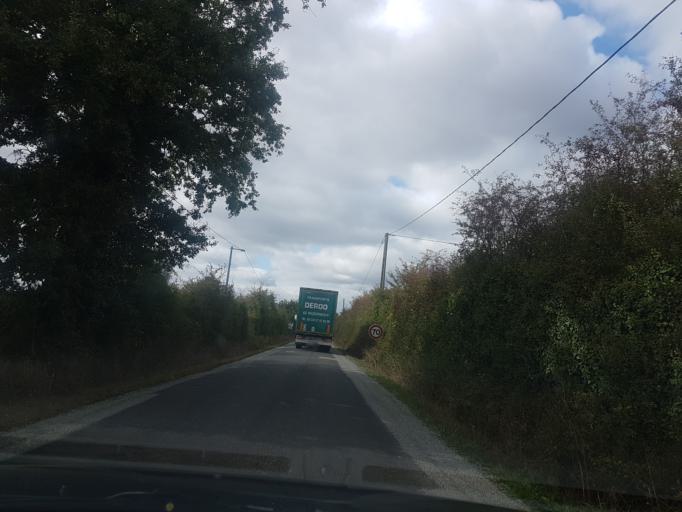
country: FR
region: Pays de la Loire
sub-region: Departement de la Loire-Atlantique
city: Saint-Mars-du-Desert
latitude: 47.3905
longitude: -1.4137
